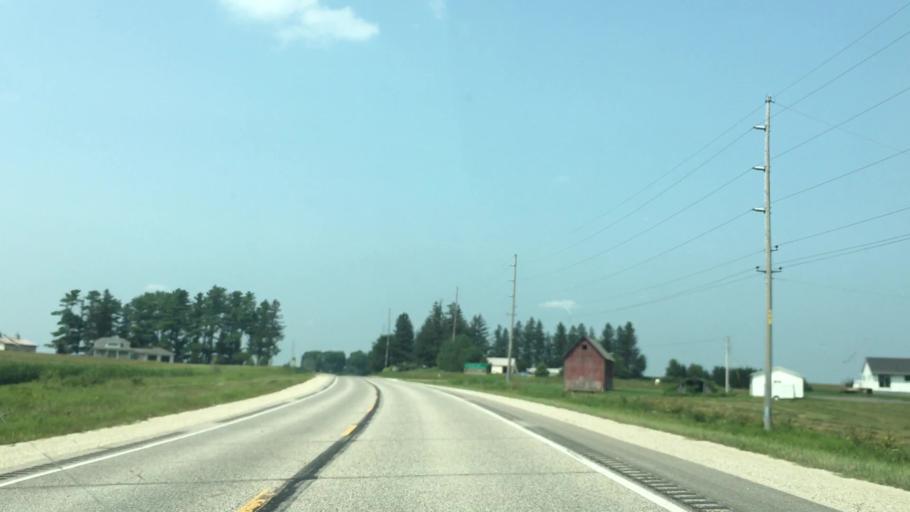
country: US
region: Iowa
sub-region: Fayette County
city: West Union
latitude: 42.9047
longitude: -91.8111
